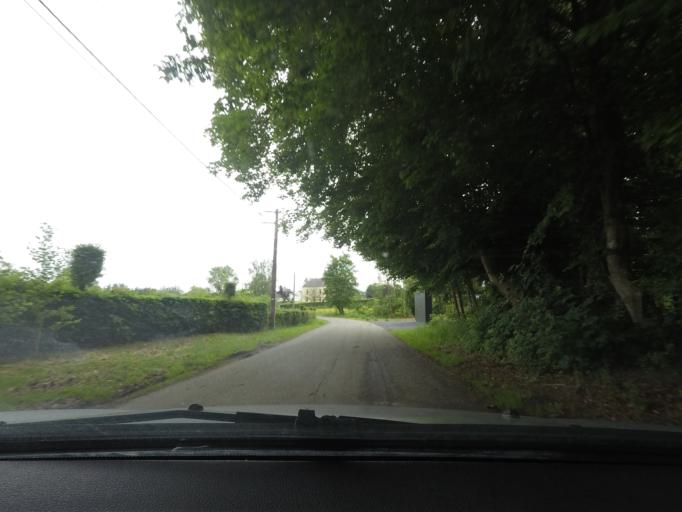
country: BE
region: Wallonia
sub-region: Province du Luxembourg
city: Leglise
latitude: 49.8158
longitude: 5.5333
